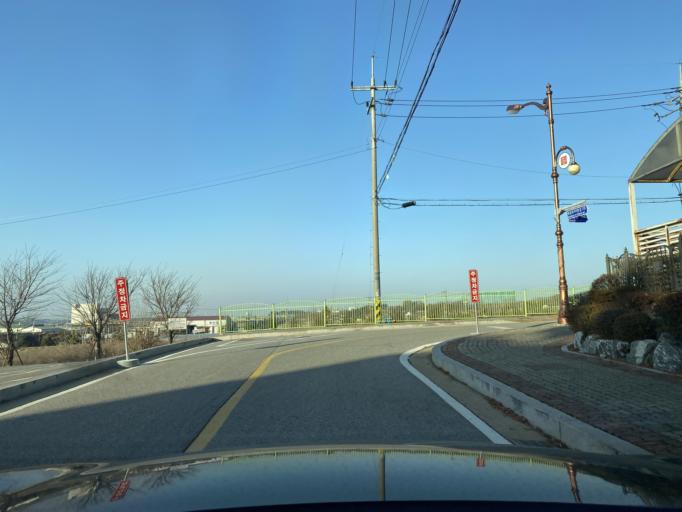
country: KR
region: Chungcheongnam-do
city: Yesan
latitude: 36.6965
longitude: 126.8313
